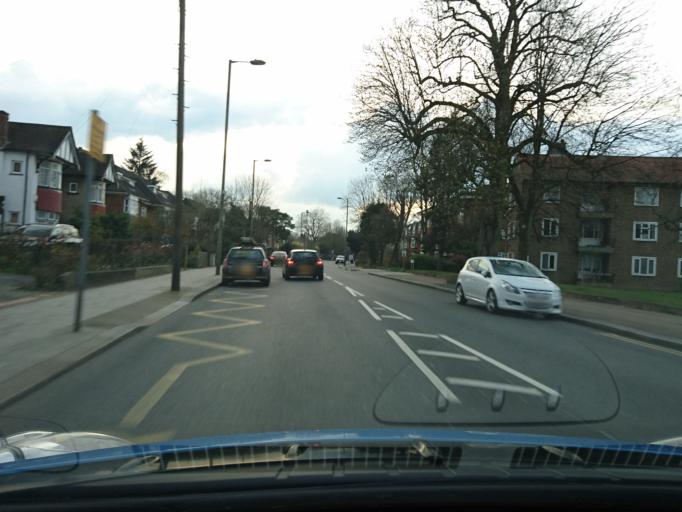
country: GB
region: England
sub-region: Greater London
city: Hadley Wood
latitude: 51.6296
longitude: -0.1675
